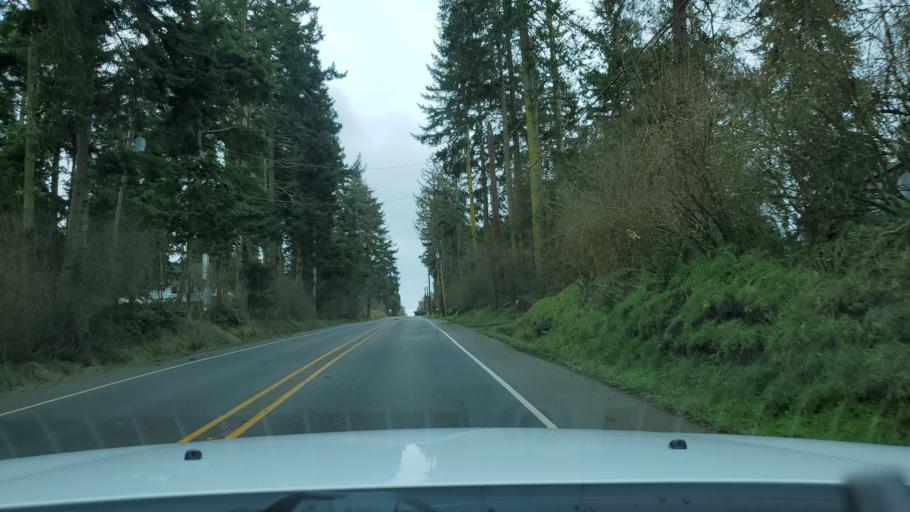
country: US
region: Washington
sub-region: Island County
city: Ault Field
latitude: 48.2933
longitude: -122.7254
